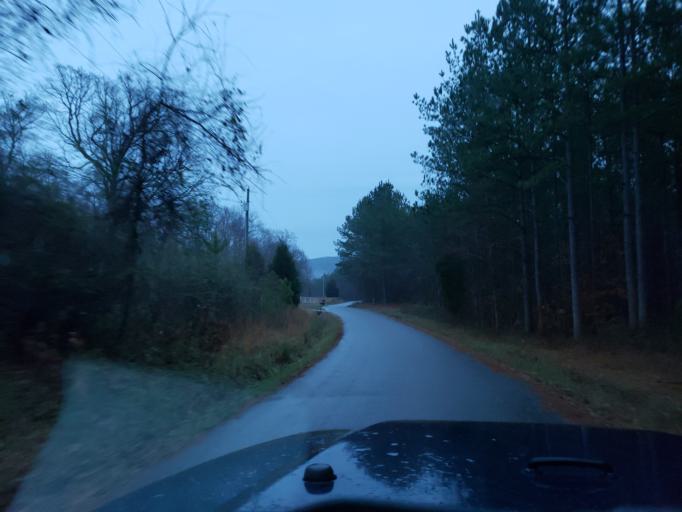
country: US
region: North Carolina
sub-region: Cleveland County
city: White Plains
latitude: 35.1484
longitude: -81.4236
